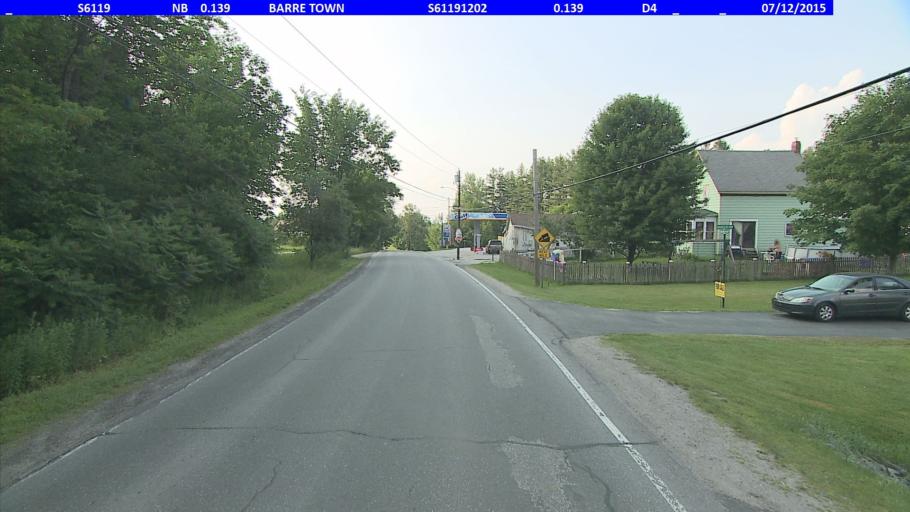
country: US
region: Vermont
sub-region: Washington County
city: South Barre
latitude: 44.1721
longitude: -72.4912
